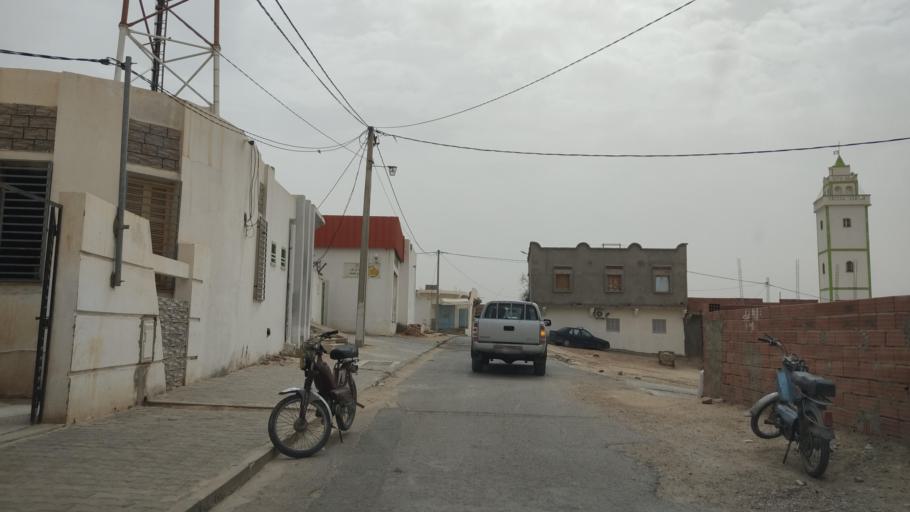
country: TN
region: Gafsa
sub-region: Gafsa Municipality
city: Gafsa
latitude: 34.3351
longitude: 8.9515
